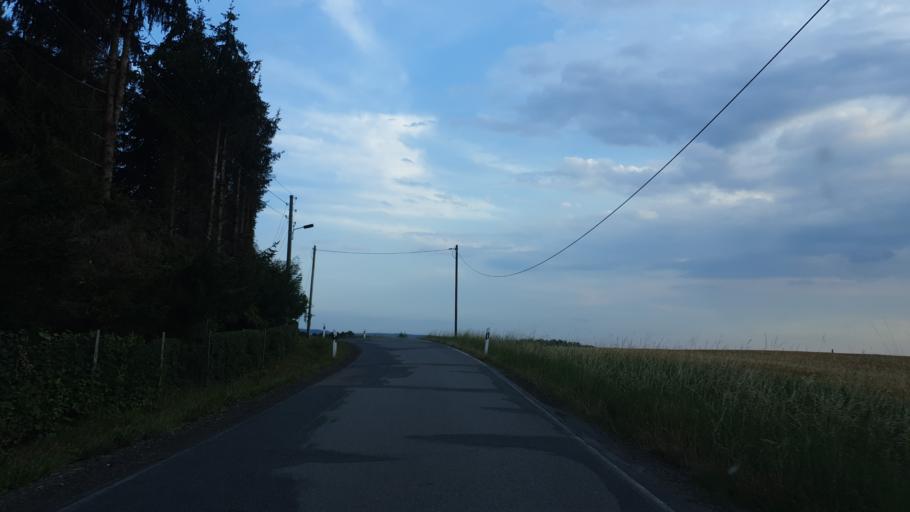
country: DE
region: Saxony
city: Lugau
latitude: 50.7484
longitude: 12.7409
